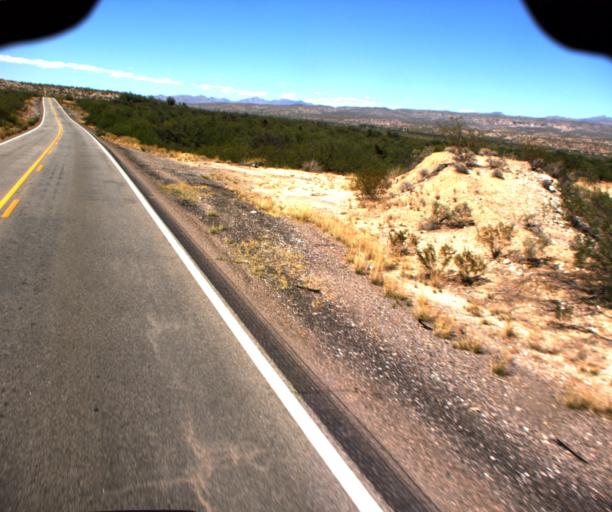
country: US
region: Arizona
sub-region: Yavapai County
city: Bagdad
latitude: 34.7818
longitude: -113.6229
